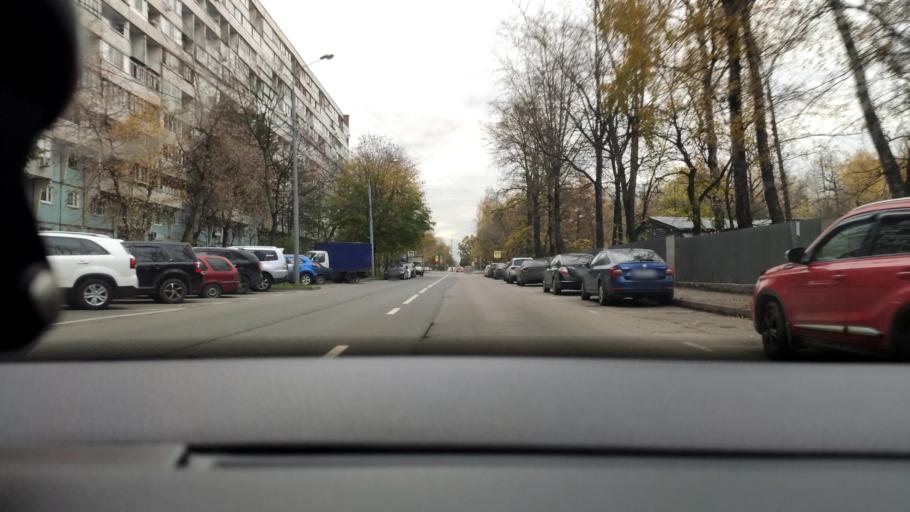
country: RU
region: Moscow
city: Lianozovo
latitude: 55.9007
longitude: 37.5740
